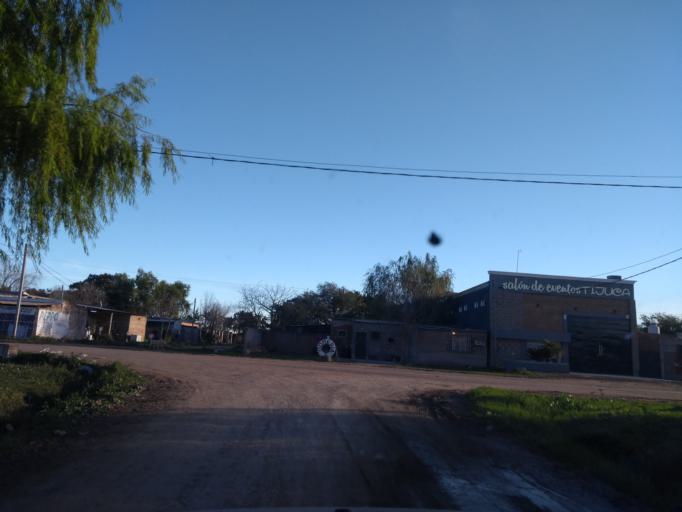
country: AR
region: Chaco
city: Puerto Vilelas
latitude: -27.4997
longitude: -58.9600
